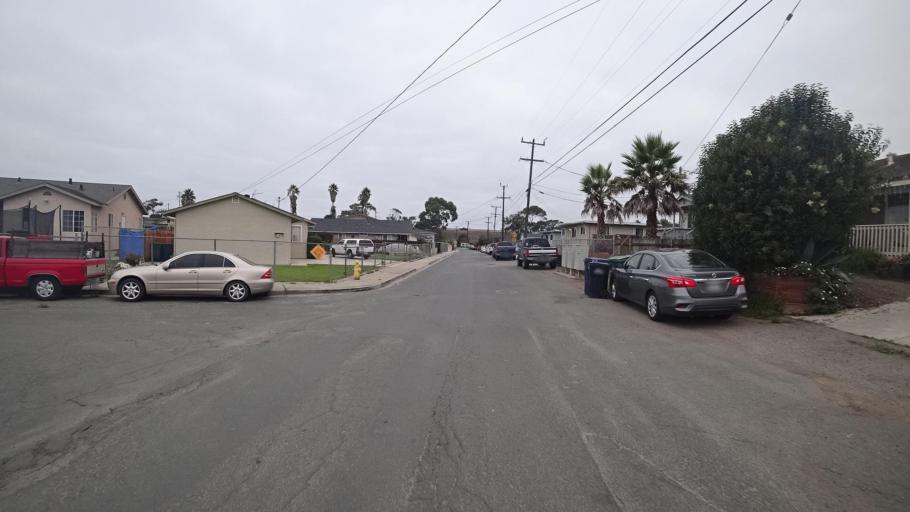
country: US
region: California
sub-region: Monterey County
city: Castroville
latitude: 36.7641
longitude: -121.7471
